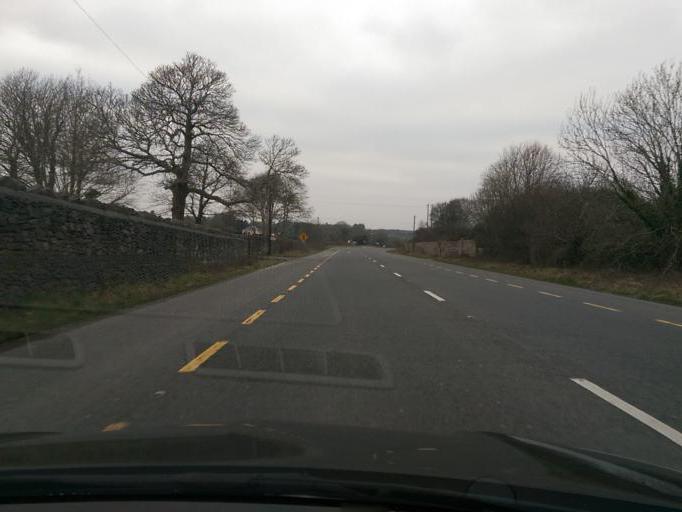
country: IE
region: Connaught
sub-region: County Galway
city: Moycullen
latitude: 53.3094
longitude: -9.1370
